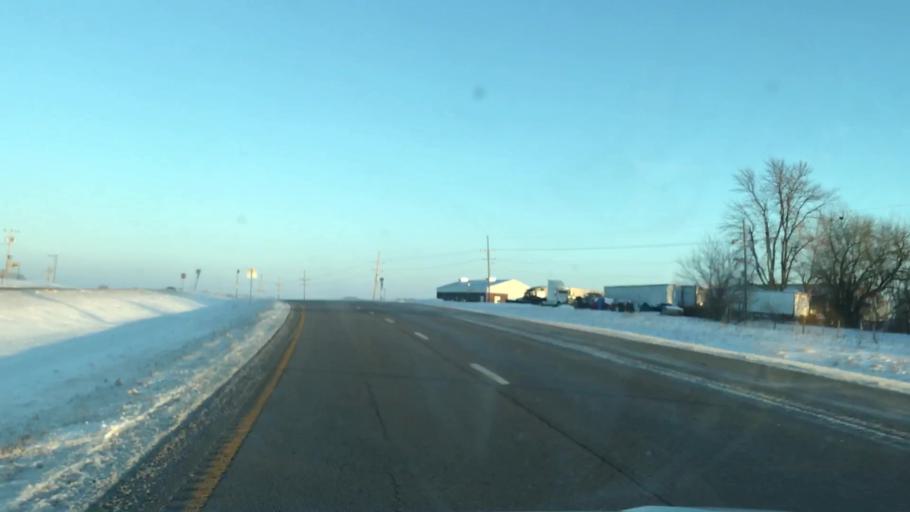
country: US
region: Missouri
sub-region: Clinton County
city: Cameron
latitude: 39.7549
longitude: -94.3392
